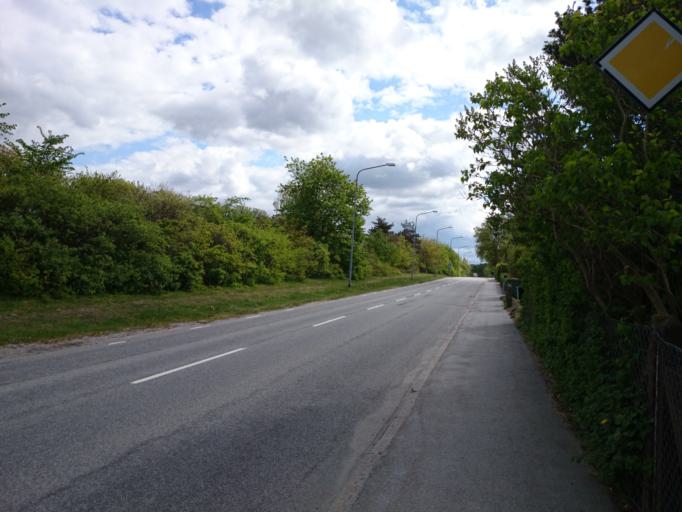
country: SE
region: Skane
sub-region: Lunds Kommun
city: Genarp
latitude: 55.5976
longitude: 13.4072
